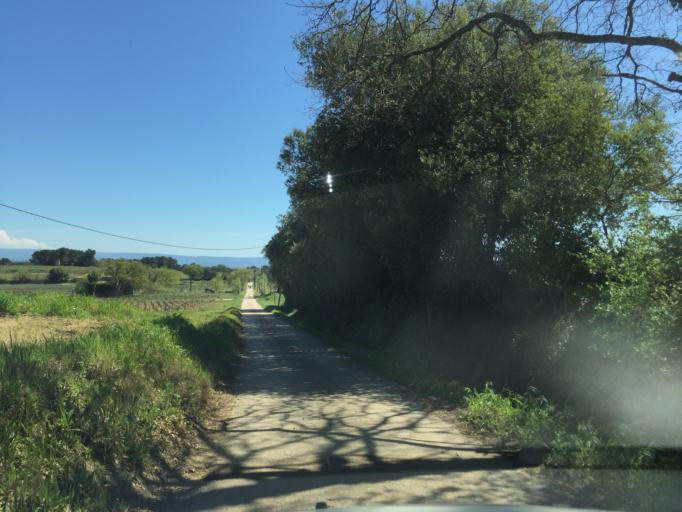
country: FR
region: Provence-Alpes-Cote d'Azur
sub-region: Departement du Vaucluse
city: Chateauneuf-du-Pape
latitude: 44.0844
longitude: 4.8470
